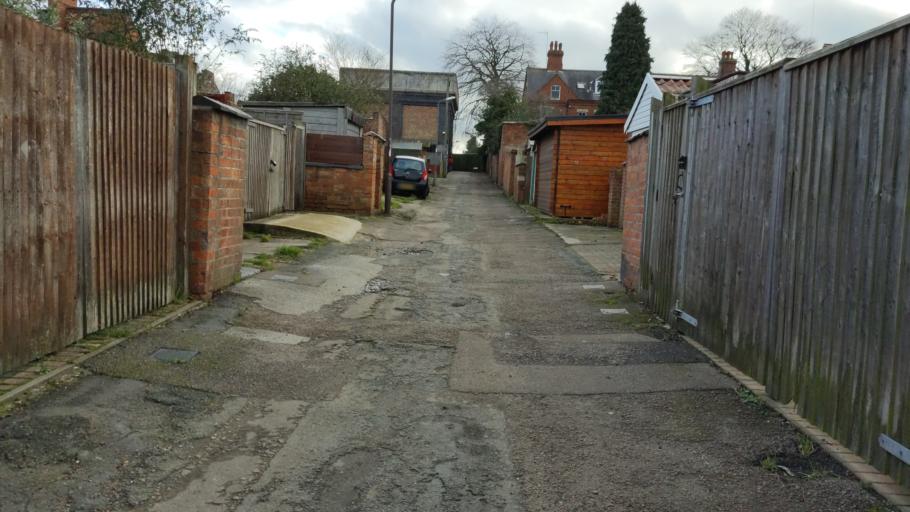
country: GB
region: England
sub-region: Milton Keynes
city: Bradwell
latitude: 52.0598
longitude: -0.8123
